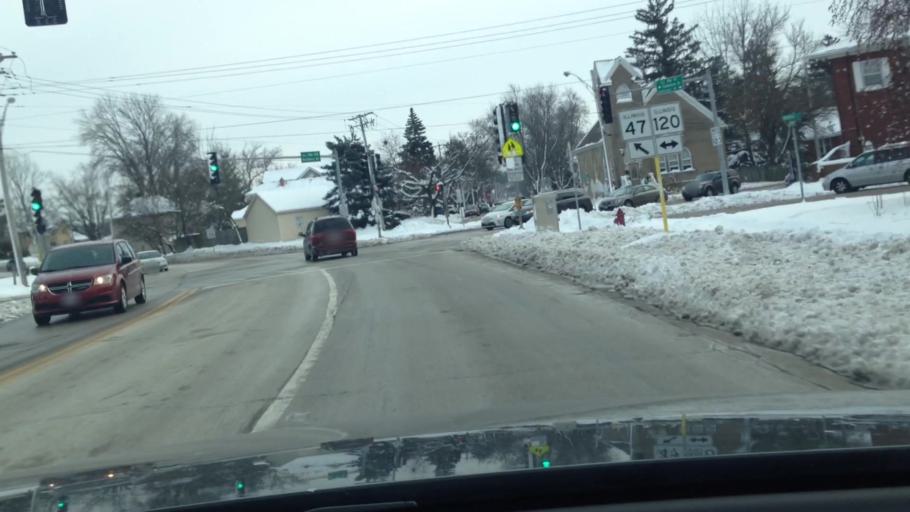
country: US
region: Illinois
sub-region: McHenry County
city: Woodstock
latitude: 42.3198
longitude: -88.4432
